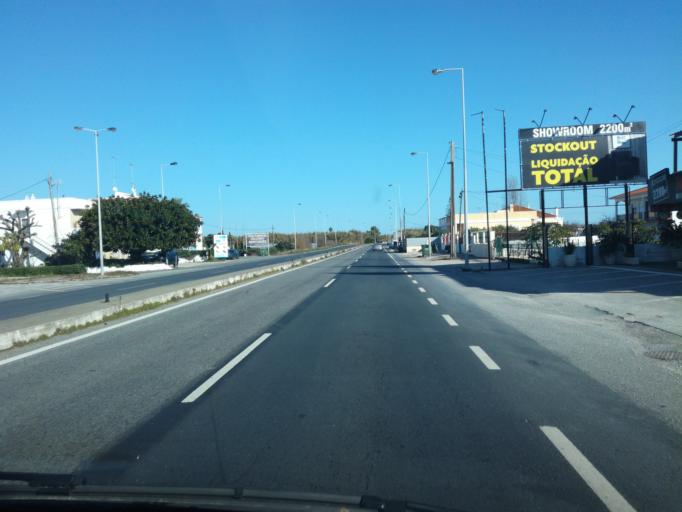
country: PT
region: Faro
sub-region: Olhao
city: Olhao
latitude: 37.0308
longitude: -7.8712
